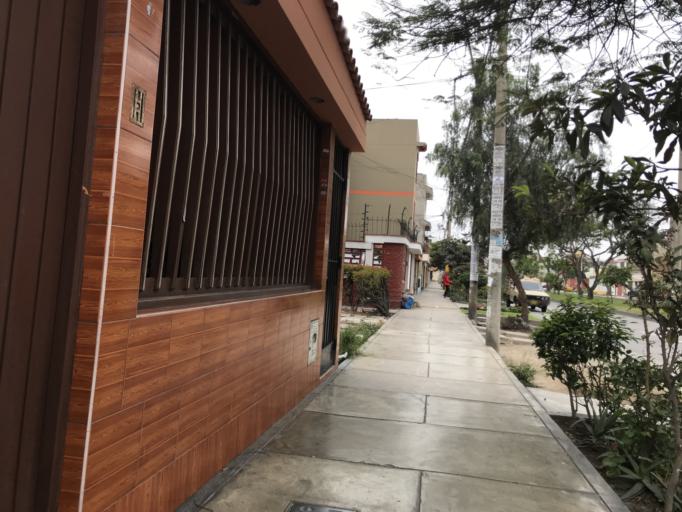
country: PE
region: Lima
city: Lima
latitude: -12.0610
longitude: -77.0669
